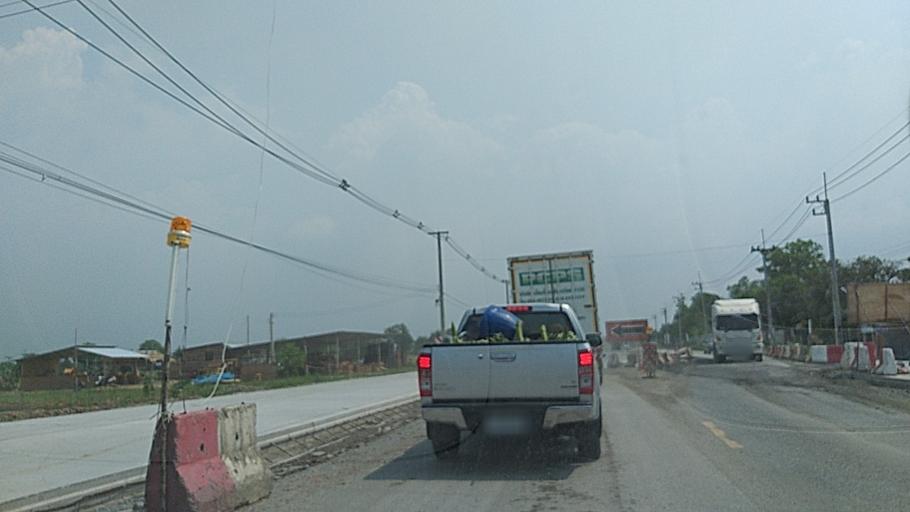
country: TH
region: Chon Buri
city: Phanat Nikhom
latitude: 13.4063
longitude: 101.1901
